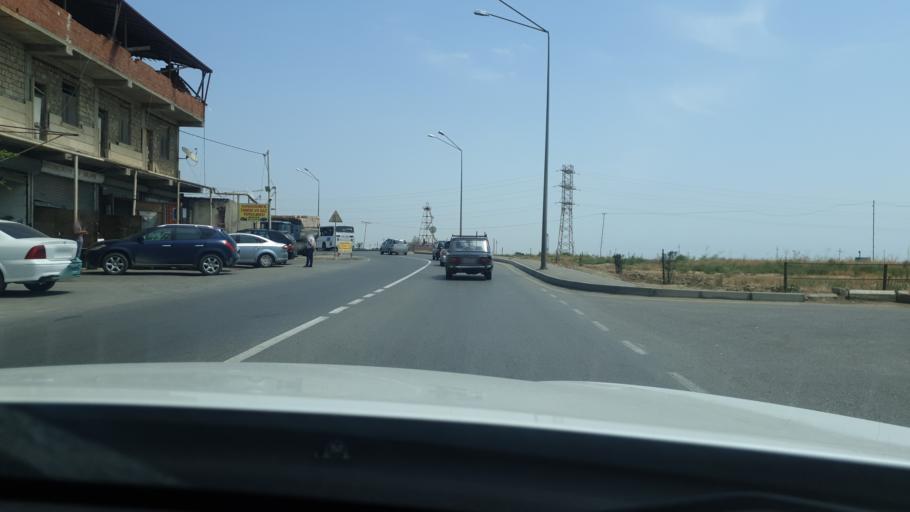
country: AZ
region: Baki
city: Qaracuxur
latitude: 40.3934
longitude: 49.9908
